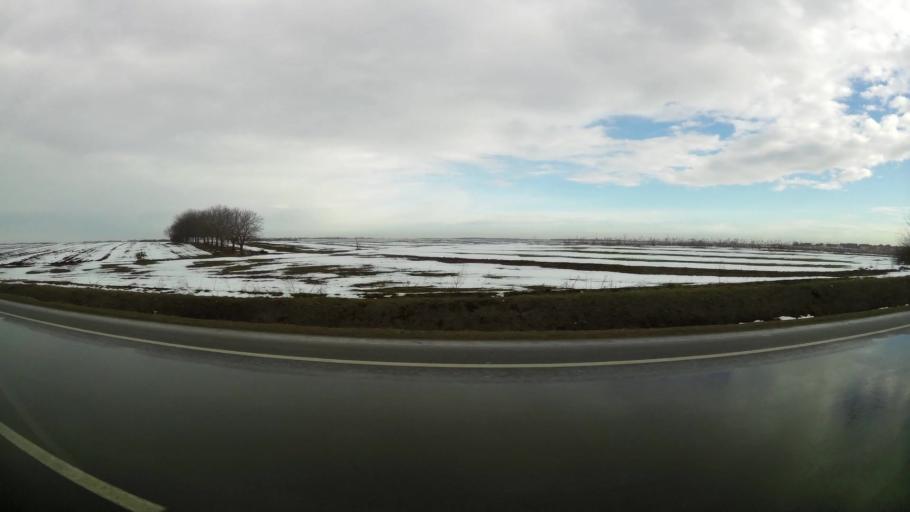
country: RS
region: Central Serbia
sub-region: Belgrade
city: Surcin
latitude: 44.8040
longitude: 20.3117
